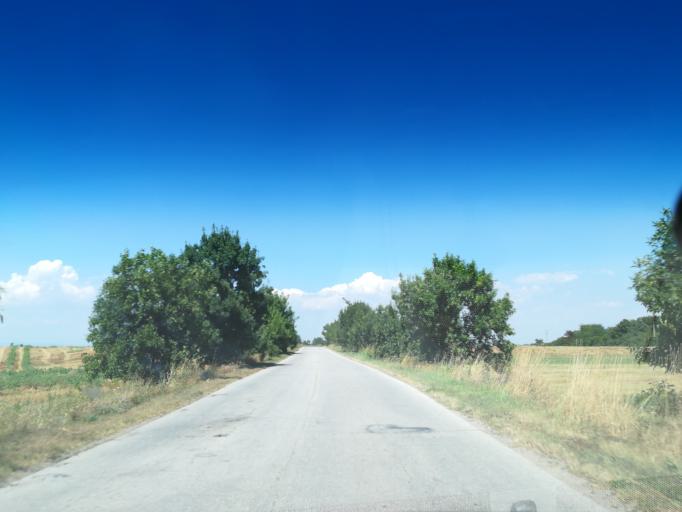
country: BG
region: Plovdiv
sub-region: Obshtina Sadovo
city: Sadovo
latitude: 42.0430
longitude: 25.1372
